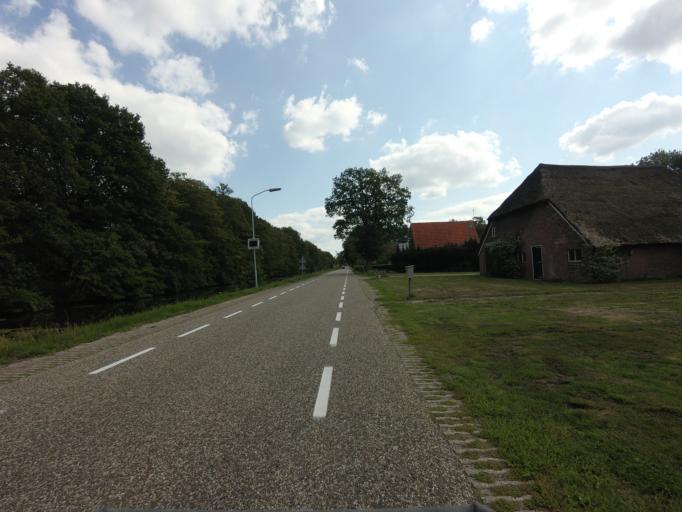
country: NL
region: Drenthe
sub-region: Gemeente Westerveld
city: Dwingeloo
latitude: 52.8685
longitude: 6.4493
